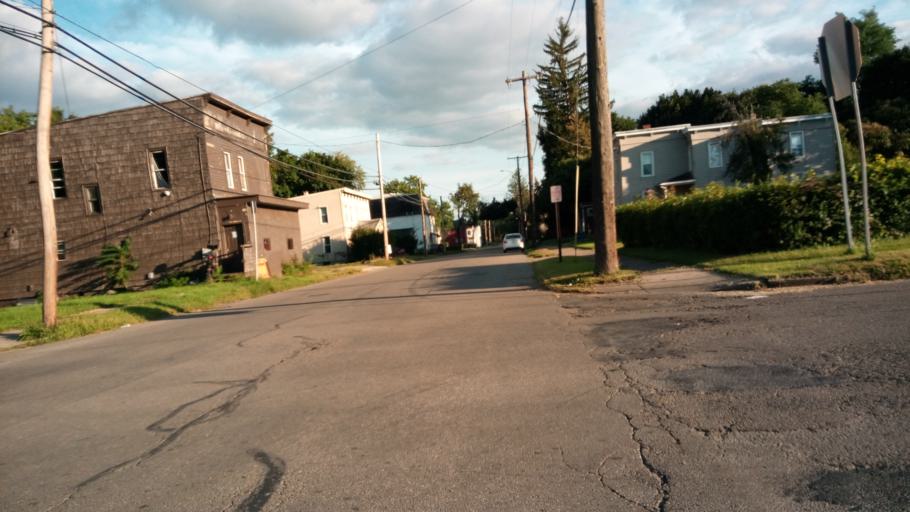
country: US
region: New York
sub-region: Chemung County
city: Elmira Heights
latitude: 42.1122
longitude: -76.8111
